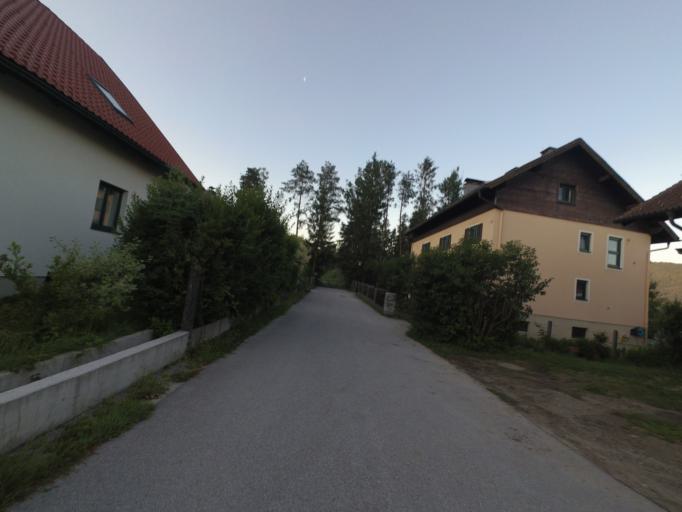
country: AT
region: Salzburg
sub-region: Politischer Bezirk Hallein
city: Puch bei Hallein
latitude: 47.7228
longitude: 13.0792
